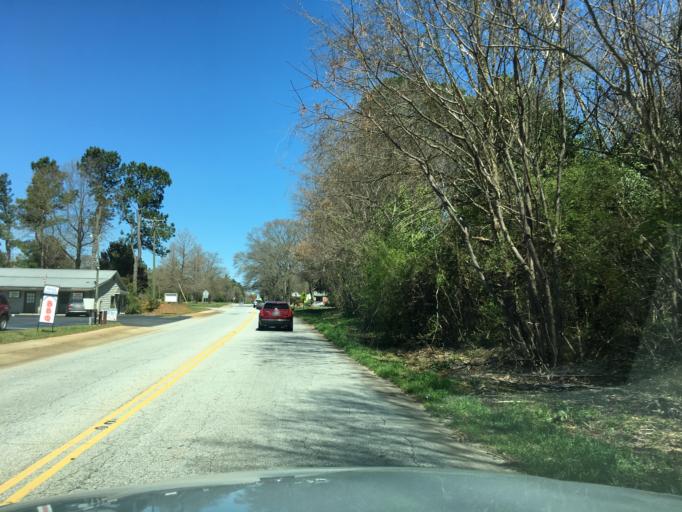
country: US
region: South Carolina
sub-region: Spartanburg County
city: Fairforest
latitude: 34.9240
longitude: -82.0015
